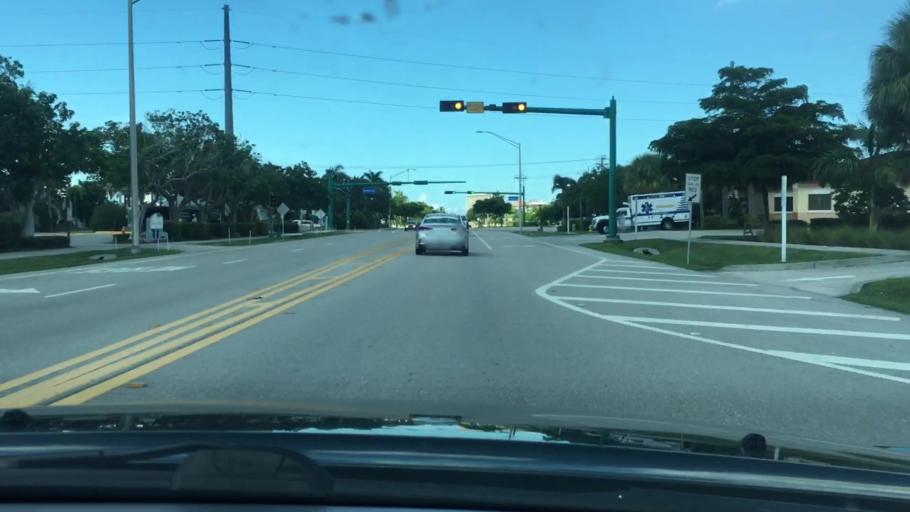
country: US
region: Florida
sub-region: Collier County
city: Marco
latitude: 25.9371
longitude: -81.7145
